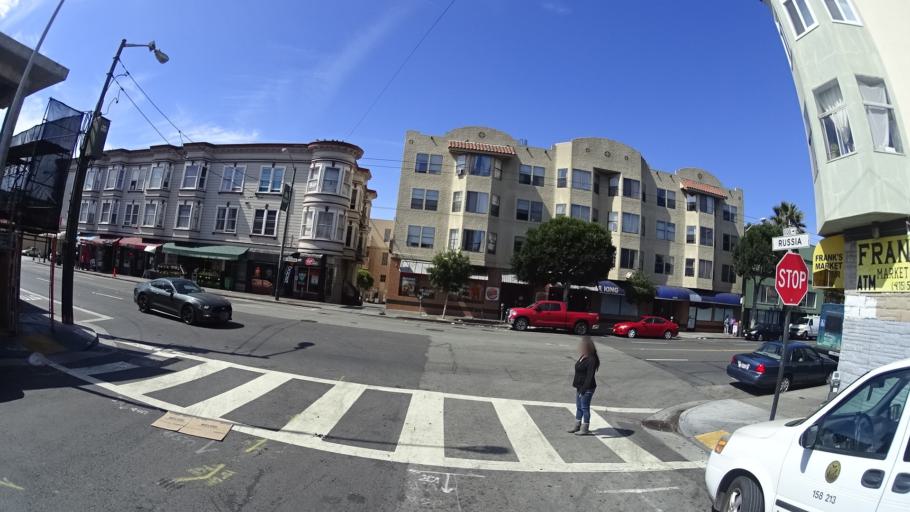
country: US
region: California
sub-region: San Mateo County
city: Daly City
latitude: 37.7215
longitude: -122.4369
